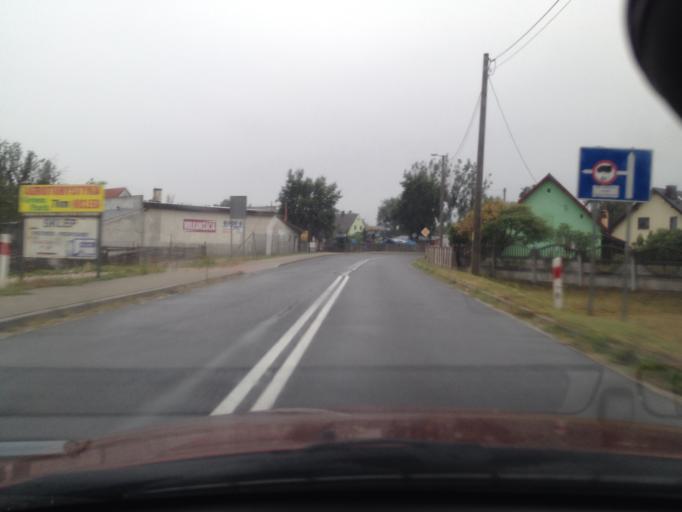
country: PL
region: Lubusz
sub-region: Powiat zaganski
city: Ilowa
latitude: 51.5307
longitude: 15.2330
